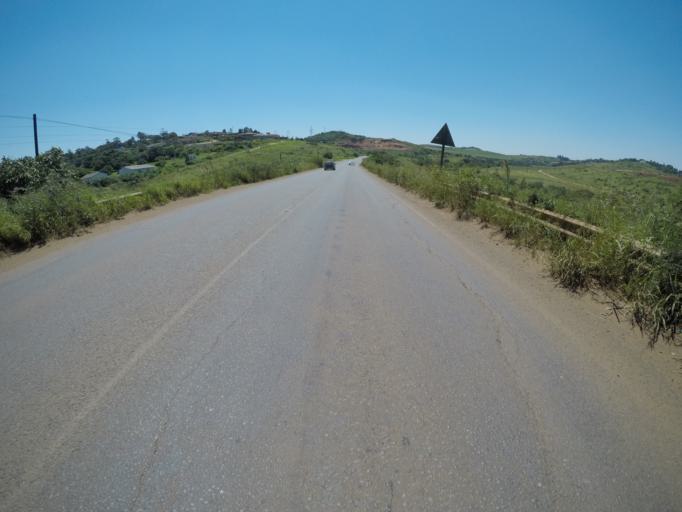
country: ZA
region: KwaZulu-Natal
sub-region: uThungulu District Municipality
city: Empangeni
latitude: -28.7601
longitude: 31.8745
